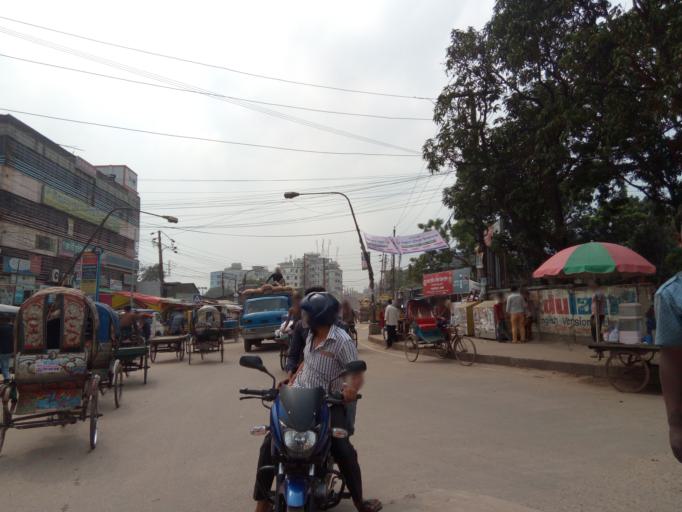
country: BD
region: Dhaka
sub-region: Dhaka
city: Dhaka
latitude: 23.6909
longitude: 90.4305
